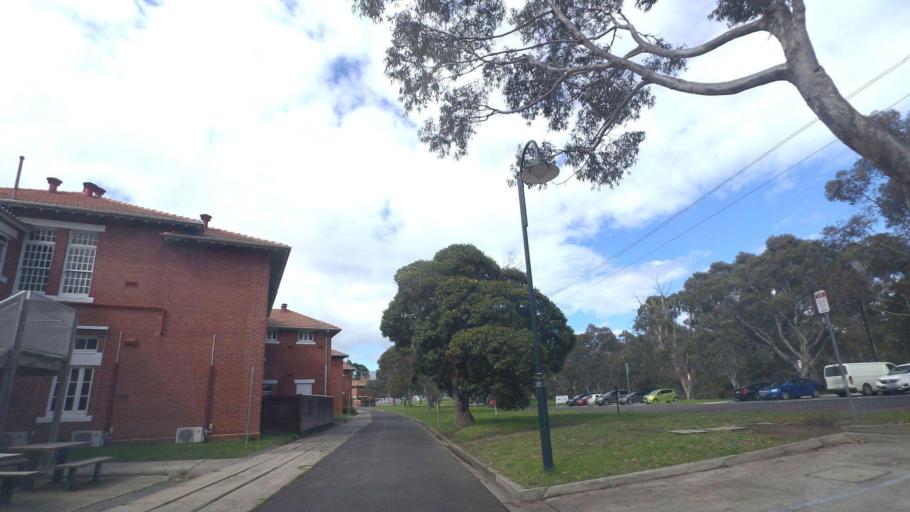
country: AU
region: Victoria
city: Macleod
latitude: -37.7207
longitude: 145.0571
